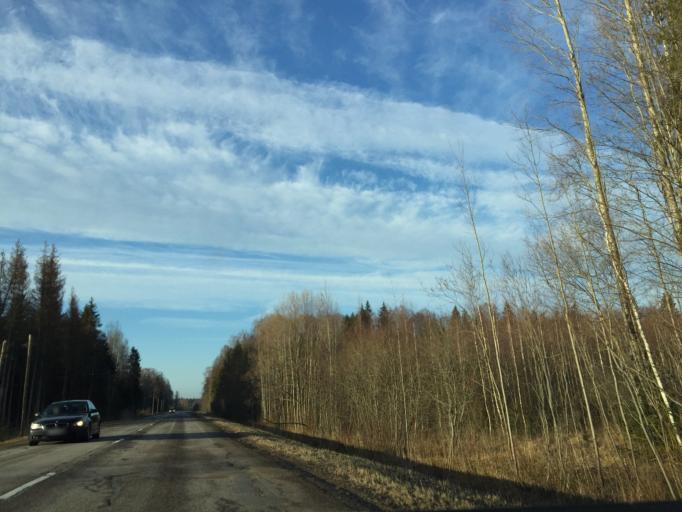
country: LV
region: Kekava
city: Balozi
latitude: 56.8061
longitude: 24.0698
